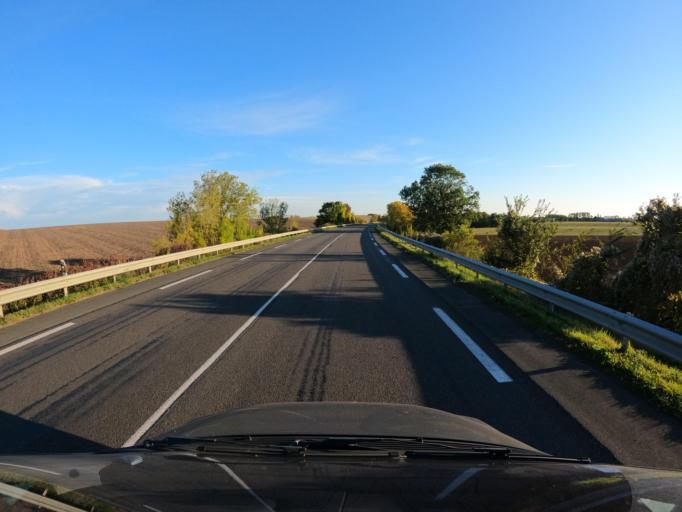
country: FR
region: Pays de la Loire
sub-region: Departement de la Vendee
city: Sainte-Hermine
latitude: 46.5663
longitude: -1.0477
